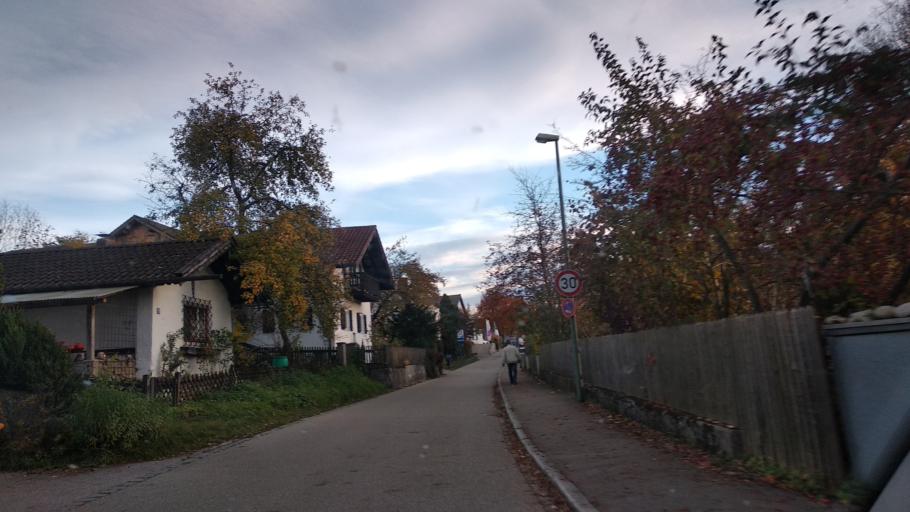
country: DE
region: Bavaria
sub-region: Upper Bavaria
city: Grafing bei Munchen
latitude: 48.0449
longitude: 11.9723
